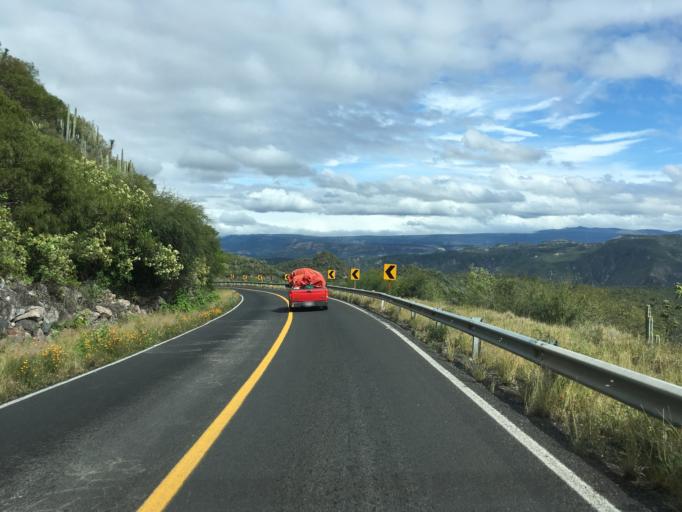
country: MX
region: Hidalgo
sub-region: San Agustin Metzquititlan
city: Mezquititlan
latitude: 20.4361
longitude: -98.6844
